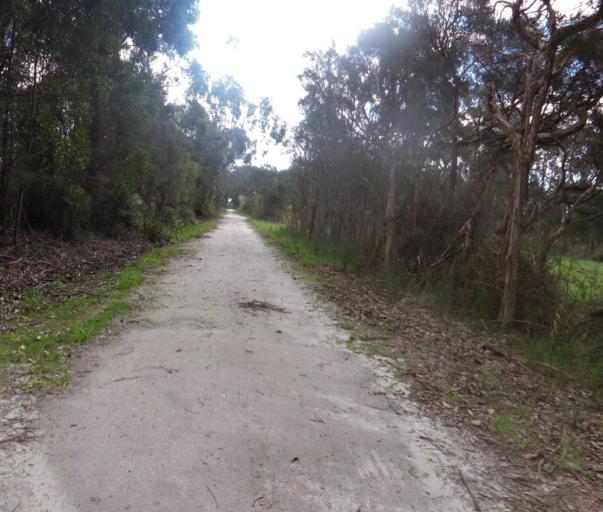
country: AU
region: Victoria
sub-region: Bass Coast
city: North Wonthaggi
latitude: -38.5949
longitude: 146.0439
